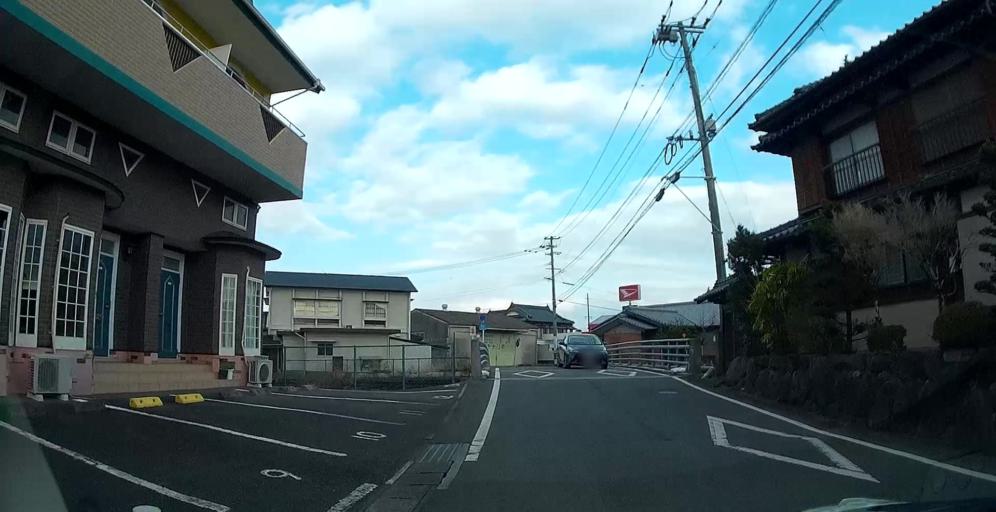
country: JP
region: Kumamoto
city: Yatsushiro
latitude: 32.5307
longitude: 130.6386
